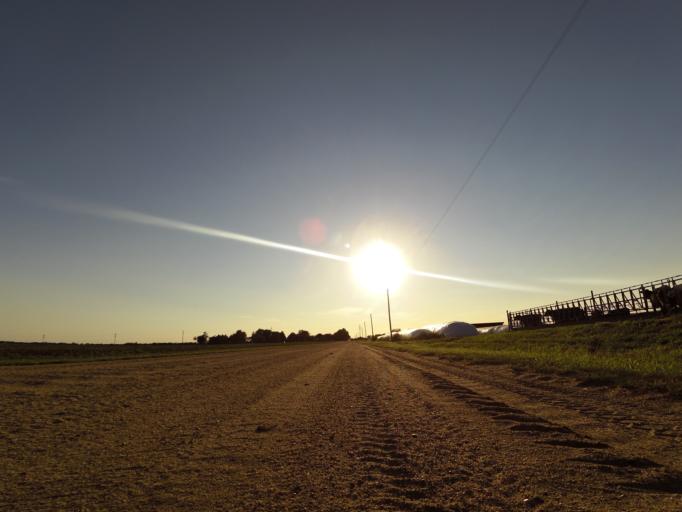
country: US
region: Kansas
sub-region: Reno County
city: South Hutchinson
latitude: 38.0136
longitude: -98.0285
